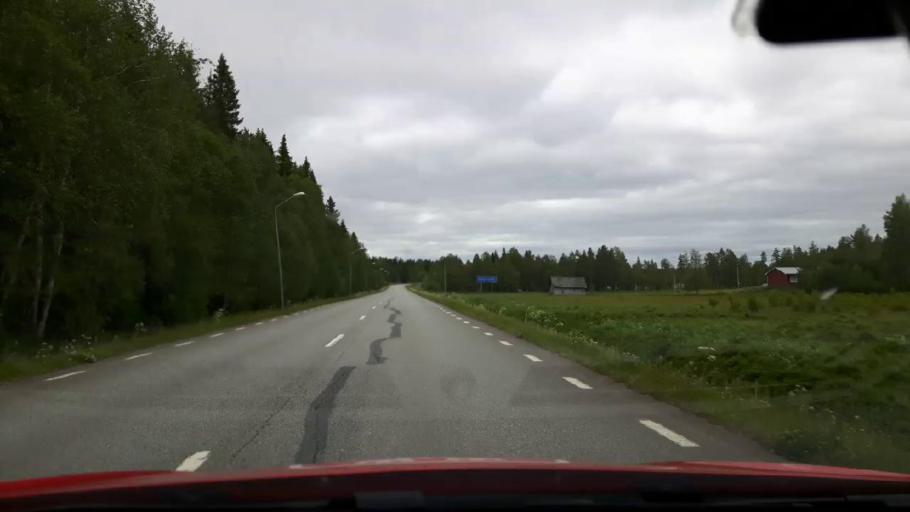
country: SE
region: Jaemtland
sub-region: Stroemsunds Kommun
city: Stroemsund
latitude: 63.5389
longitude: 15.4374
